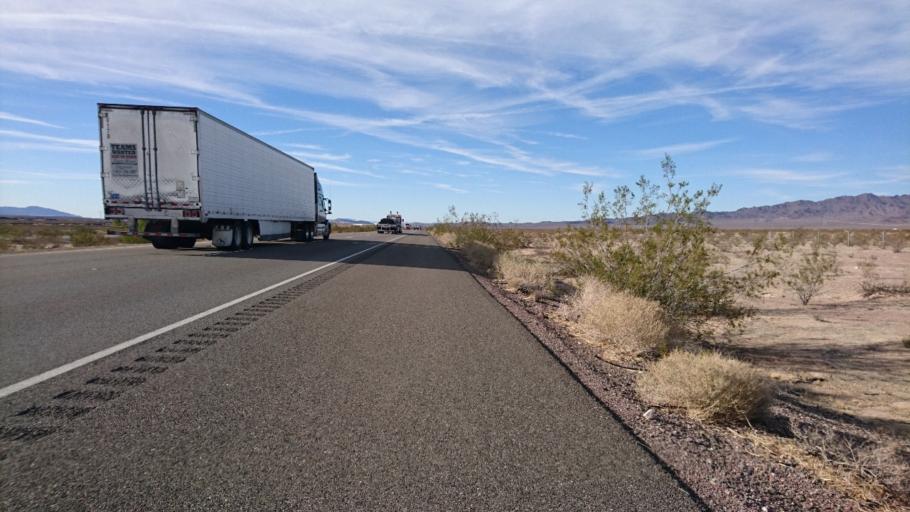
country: US
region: California
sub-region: San Bernardino County
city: Fort Irwin
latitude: 34.7639
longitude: -116.3536
